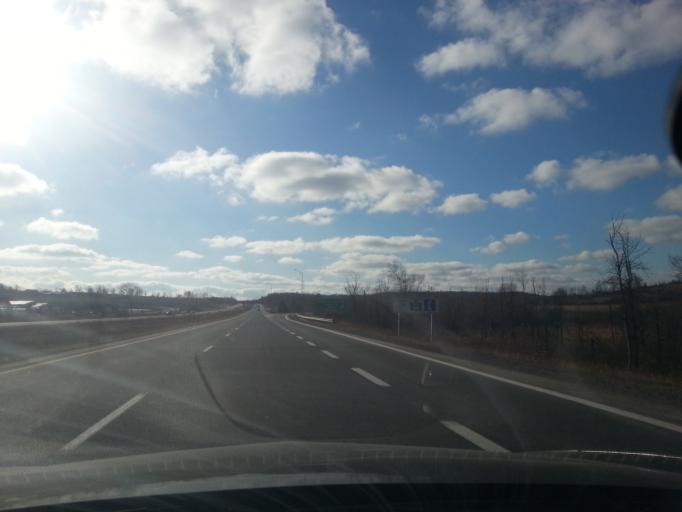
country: CA
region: Ontario
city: Omemee
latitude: 44.1908
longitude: -78.4587
